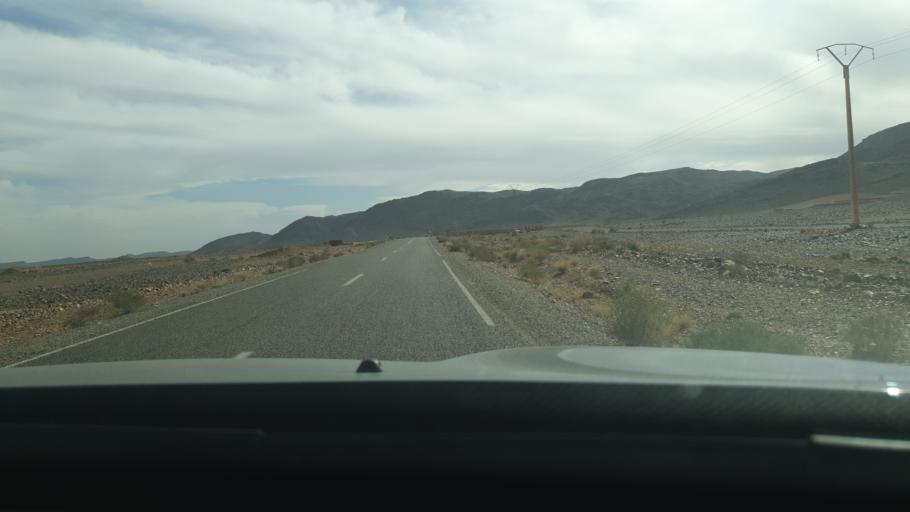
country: MA
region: Meknes-Tafilalet
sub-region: Errachidia
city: Fezna
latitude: 31.5318
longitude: -4.6405
